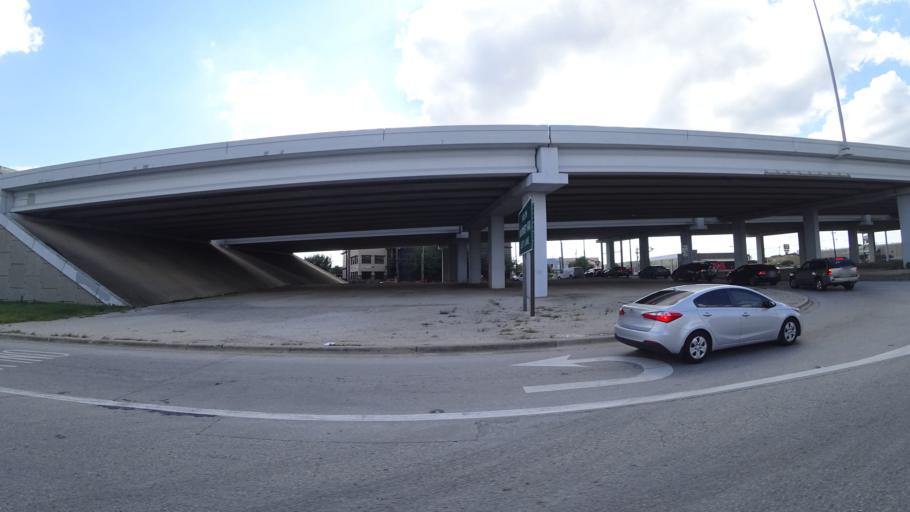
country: US
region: Texas
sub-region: Travis County
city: Wells Branch
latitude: 30.3725
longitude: -97.7239
